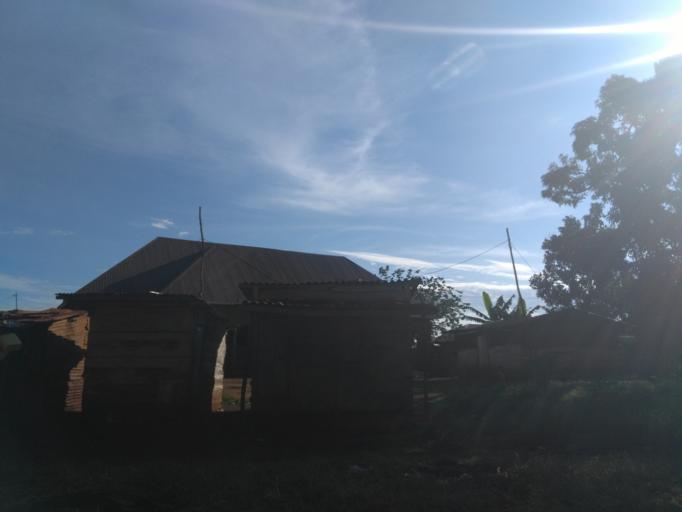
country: UG
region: Eastern Region
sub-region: Jinja District
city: Jinja
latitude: 0.4576
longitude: 33.1850
